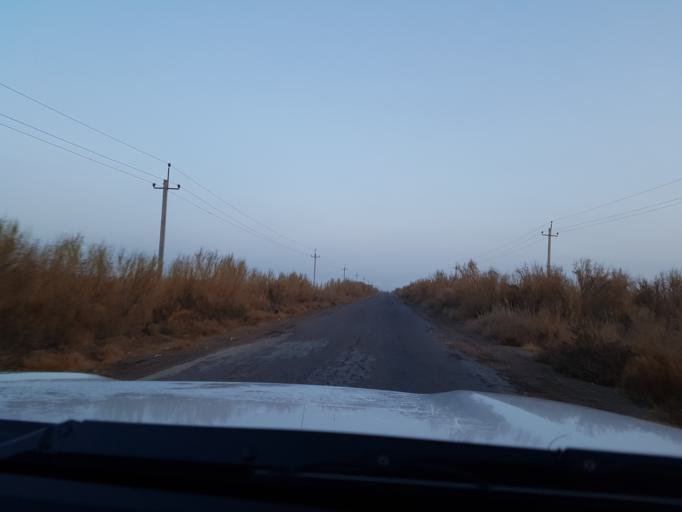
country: TM
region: Dasoguz
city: Koeneuergench
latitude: 41.7842
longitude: 58.6972
